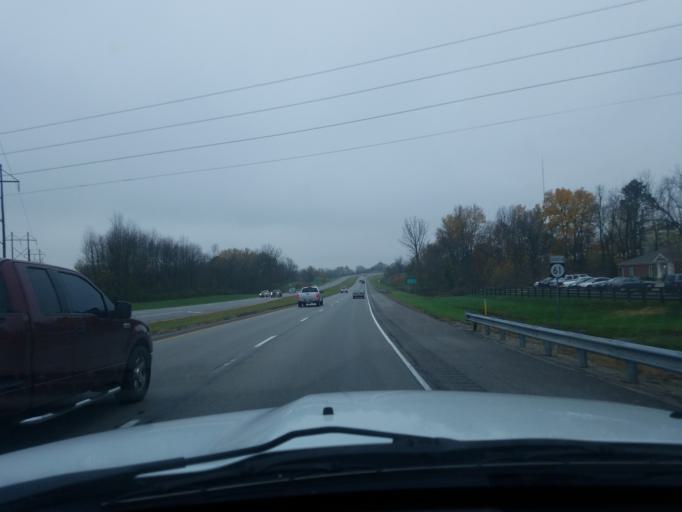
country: US
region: Kentucky
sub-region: Hardin County
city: Elizabethtown
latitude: 37.6652
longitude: -85.8397
